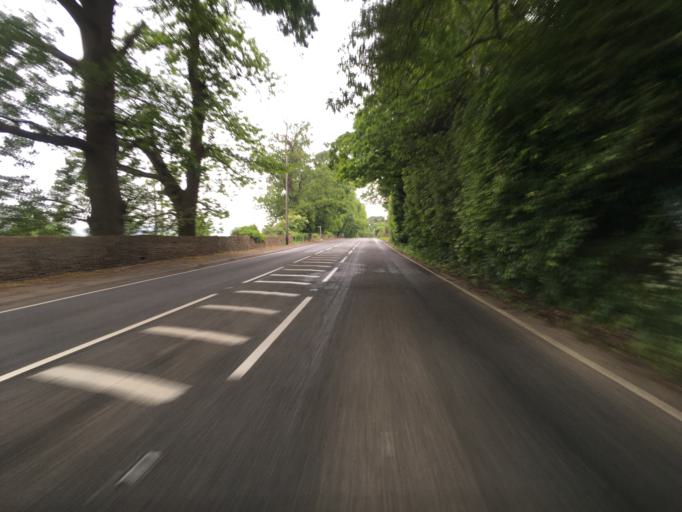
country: GB
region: England
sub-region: North Somerset
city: Brockley
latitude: 51.4014
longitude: -2.7546
